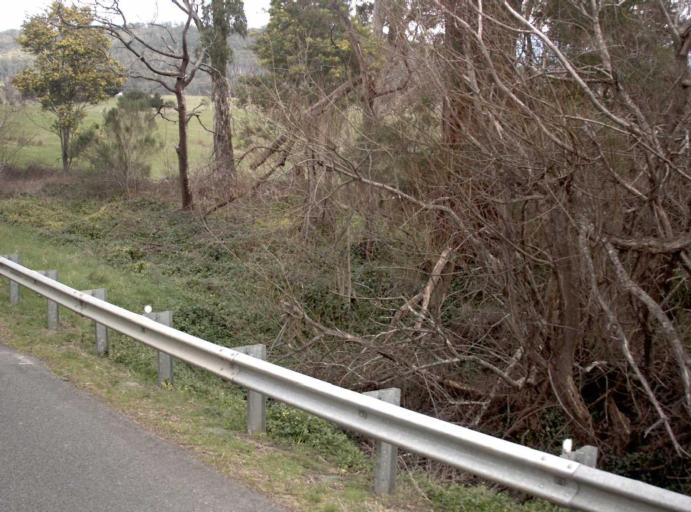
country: AU
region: Tasmania
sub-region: Launceston
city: Mayfield
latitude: -41.2065
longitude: 147.1177
